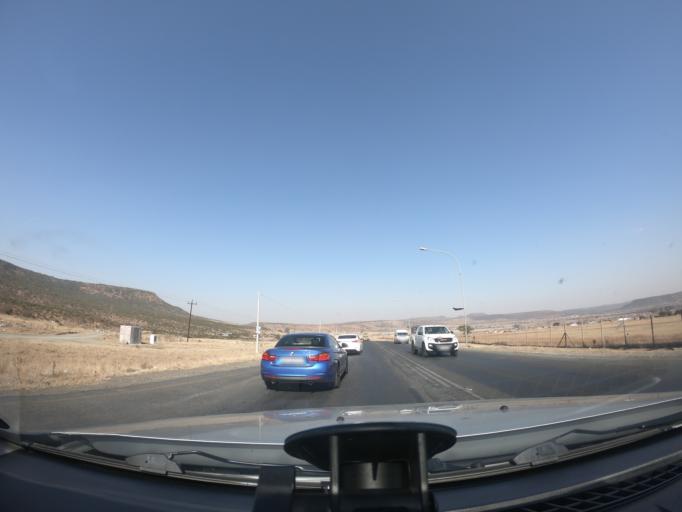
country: ZA
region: KwaZulu-Natal
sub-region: uThukela District Municipality
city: Ladysmith
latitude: -28.5722
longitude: 29.8341
